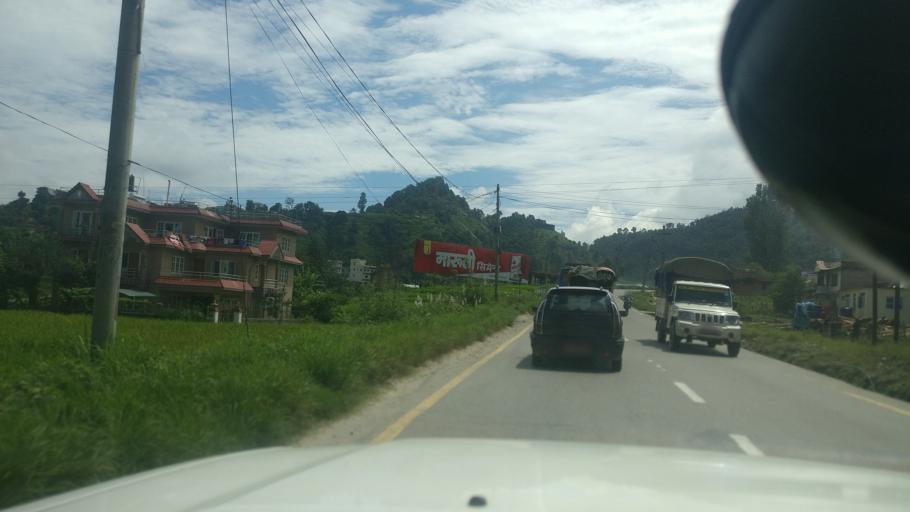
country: NP
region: Central Region
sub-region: Bagmati Zone
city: kankrabari Dovan
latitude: 27.6487
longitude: 85.4639
